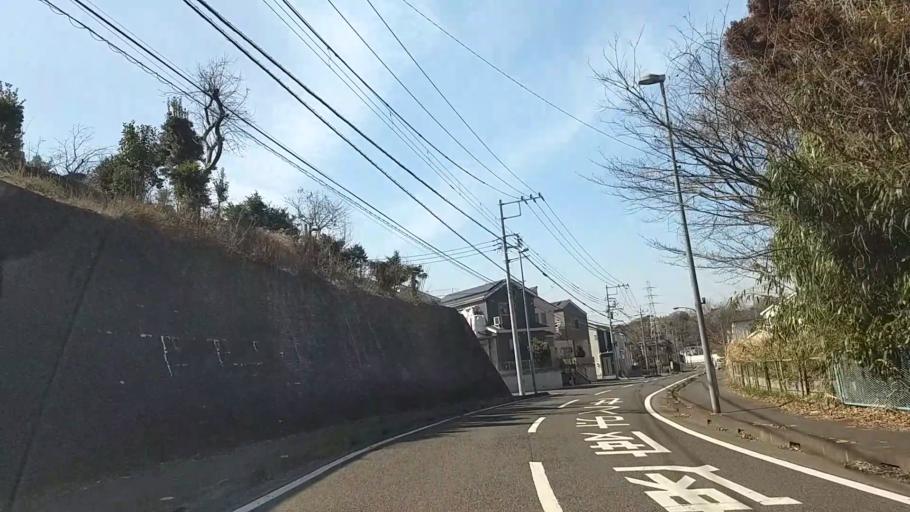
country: JP
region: Kanagawa
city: Fujisawa
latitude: 35.3820
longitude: 139.4343
